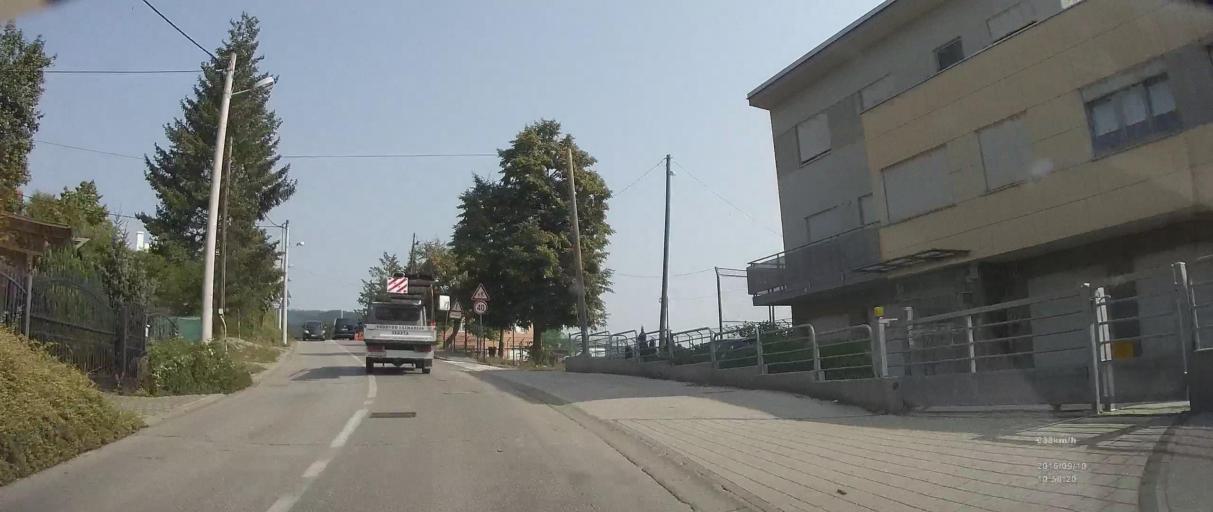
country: HR
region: Grad Zagreb
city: Zagreb
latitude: 45.8463
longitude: 15.9382
